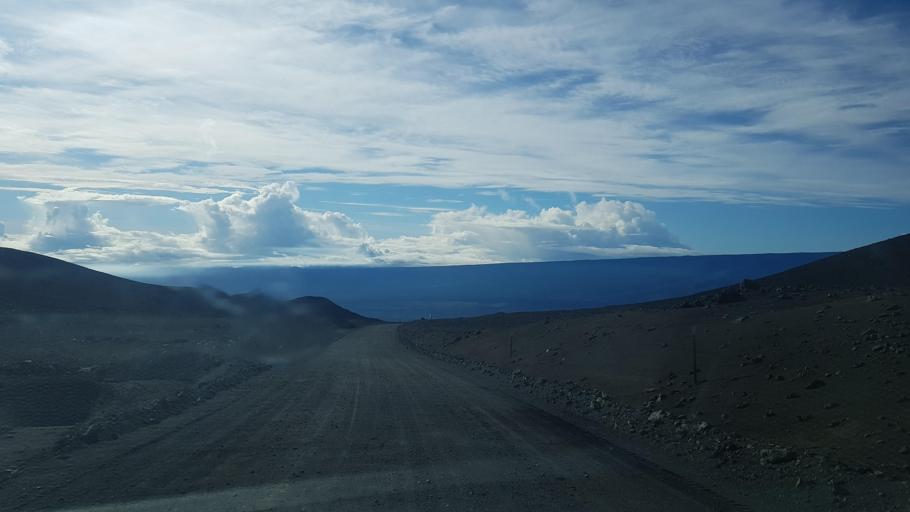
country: US
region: Hawaii
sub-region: Hawaii County
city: Honoka'a
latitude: 19.7853
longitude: -155.4544
